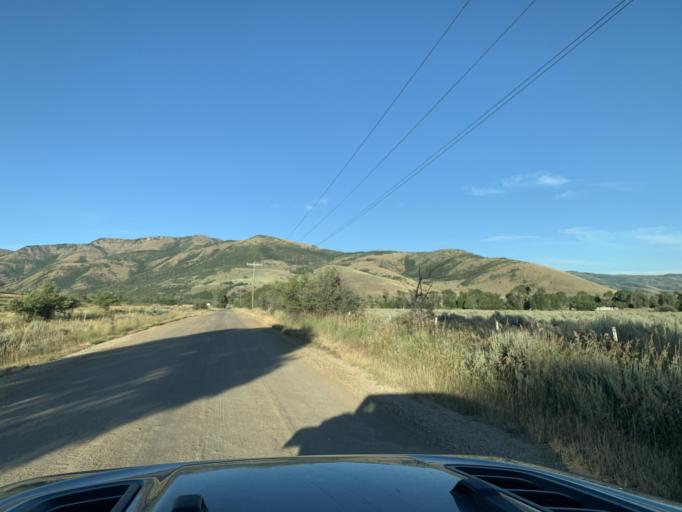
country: US
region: Utah
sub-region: Weber County
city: Wolf Creek
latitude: 41.2931
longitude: -111.7667
